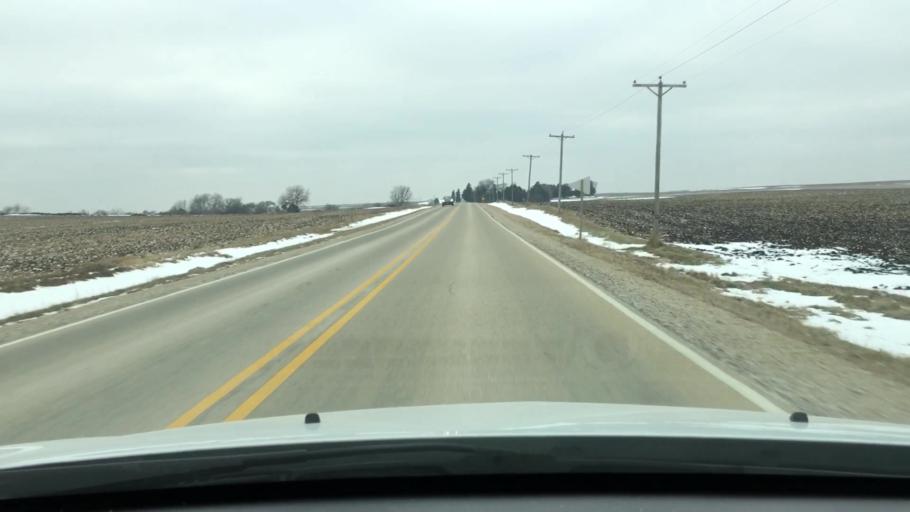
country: US
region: Illinois
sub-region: DeKalb County
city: Malta
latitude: 41.8485
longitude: -88.9316
